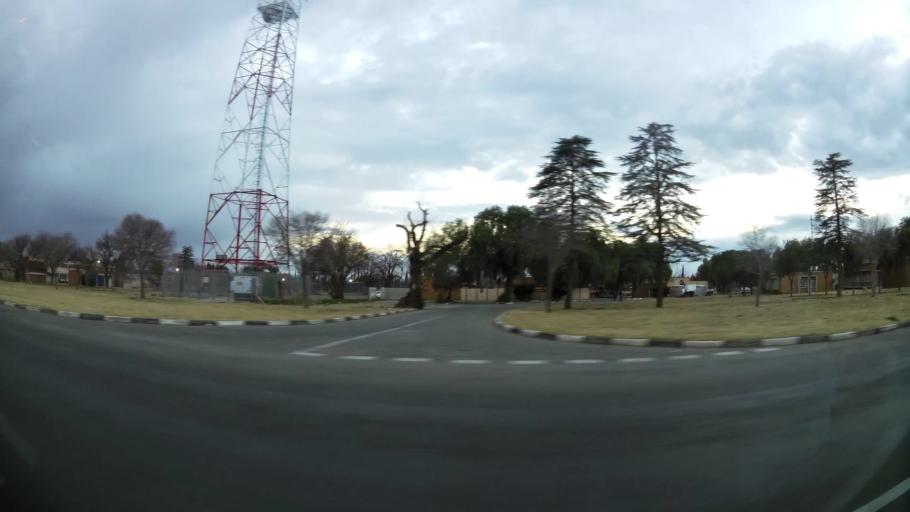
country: ZA
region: Orange Free State
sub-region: Lejweleputswa District Municipality
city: Welkom
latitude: -27.9763
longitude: 26.7450
